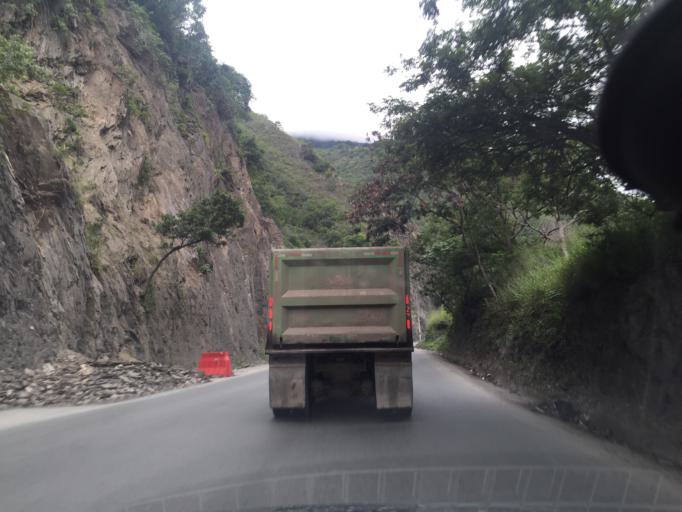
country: CO
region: Valle del Cauca
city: Dagua
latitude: 3.7779
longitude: -76.7059
